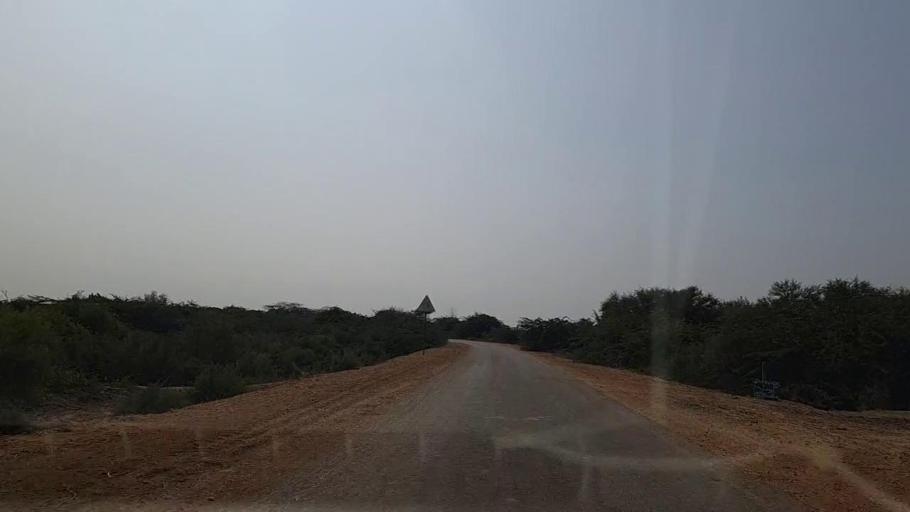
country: PK
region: Sindh
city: Chuhar Jamali
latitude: 24.2666
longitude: 67.9099
